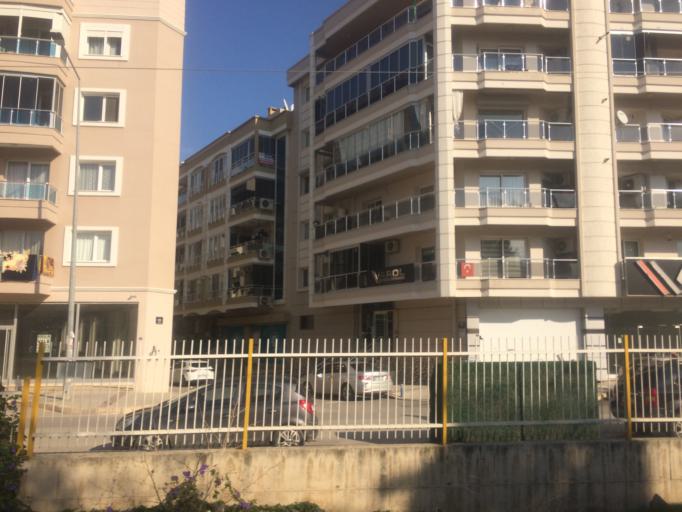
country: TR
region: Izmir
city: Karsiyaka
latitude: 38.4695
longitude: 27.0952
